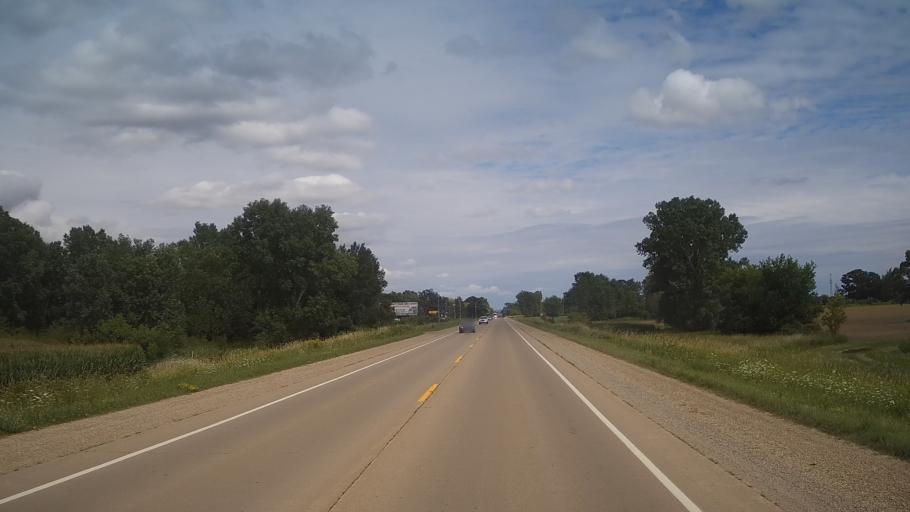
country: US
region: Wisconsin
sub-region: Winnebago County
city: Omro
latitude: 44.0332
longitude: -88.6439
